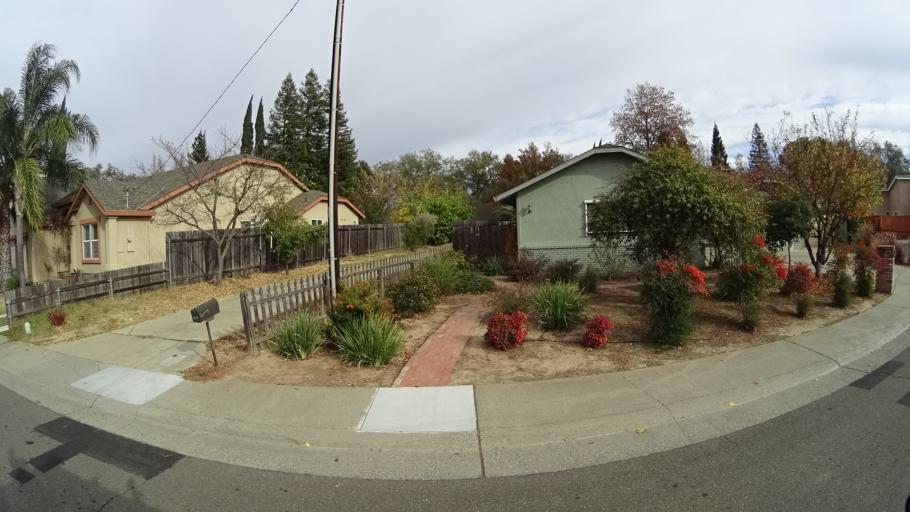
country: US
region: California
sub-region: Sacramento County
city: Citrus Heights
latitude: 38.7045
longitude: -121.2684
